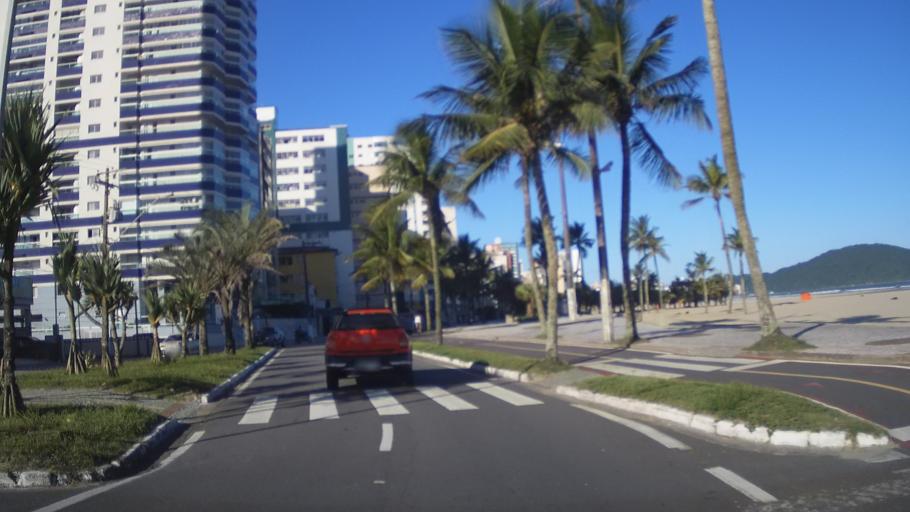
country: BR
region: Sao Paulo
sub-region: Praia Grande
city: Praia Grande
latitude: -24.0165
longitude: -46.4339
